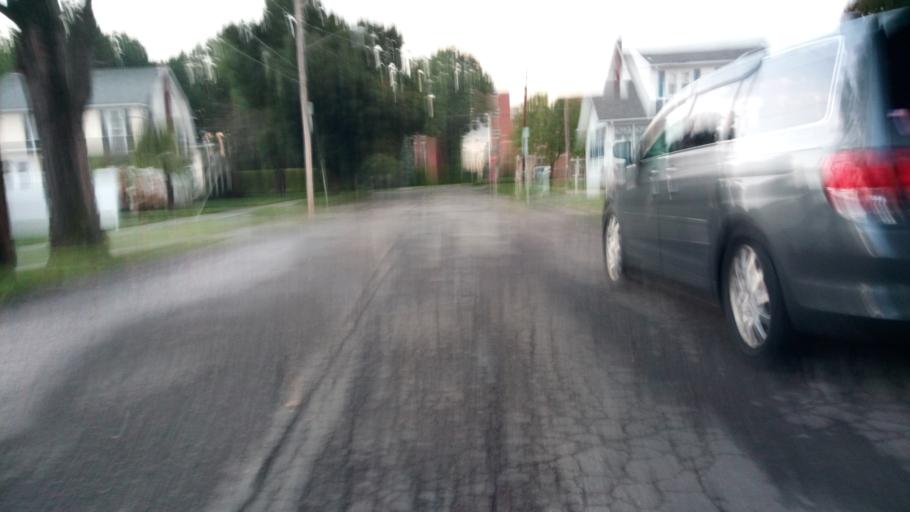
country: US
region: New York
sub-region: Chemung County
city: Elmira
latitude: 42.0984
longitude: -76.8274
